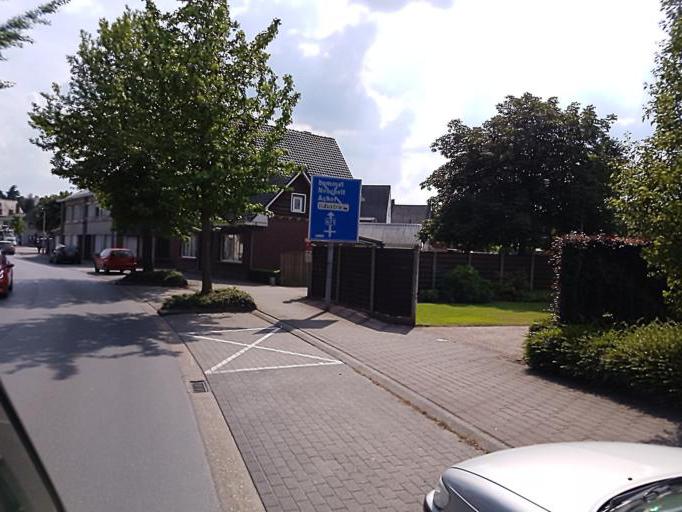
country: NL
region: North Brabant
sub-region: Gemeente Cranendonck
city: Cranendonck
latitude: 51.2519
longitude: 5.5429
